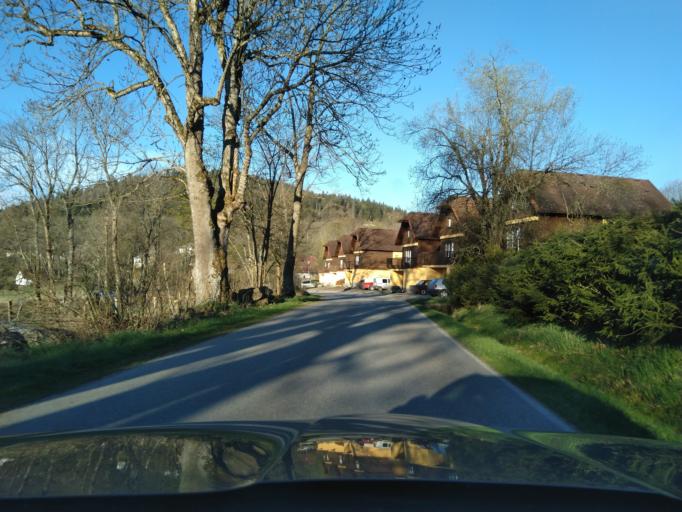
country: DE
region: Bavaria
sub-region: Lower Bavaria
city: Haidmuhle
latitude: 48.8802
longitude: 13.7785
